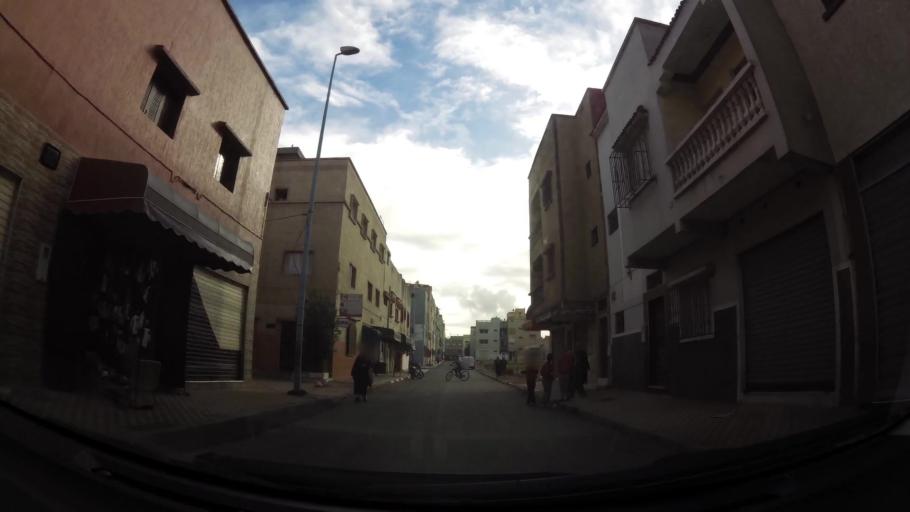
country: MA
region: Doukkala-Abda
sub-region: El-Jadida
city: El Jadida
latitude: 33.2434
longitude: -8.5279
